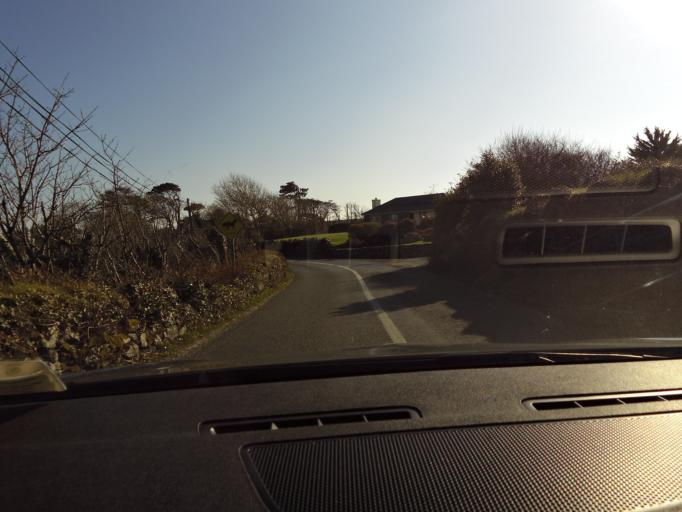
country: IE
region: Connaught
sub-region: County Galway
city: Clifden
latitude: 53.4760
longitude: -10.0200
